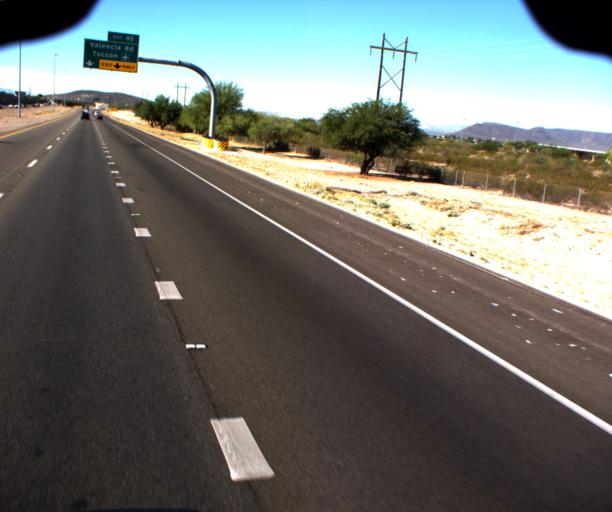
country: US
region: Arizona
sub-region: Pima County
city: Drexel Heights
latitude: 32.1455
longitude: -110.9868
